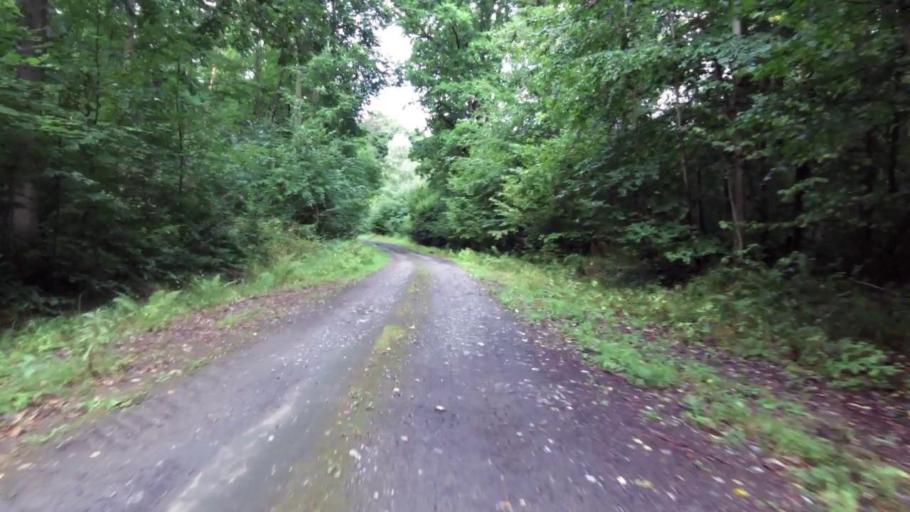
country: PL
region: West Pomeranian Voivodeship
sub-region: Powiat mysliborski
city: Debno
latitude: 52.8687
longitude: 14.6946
